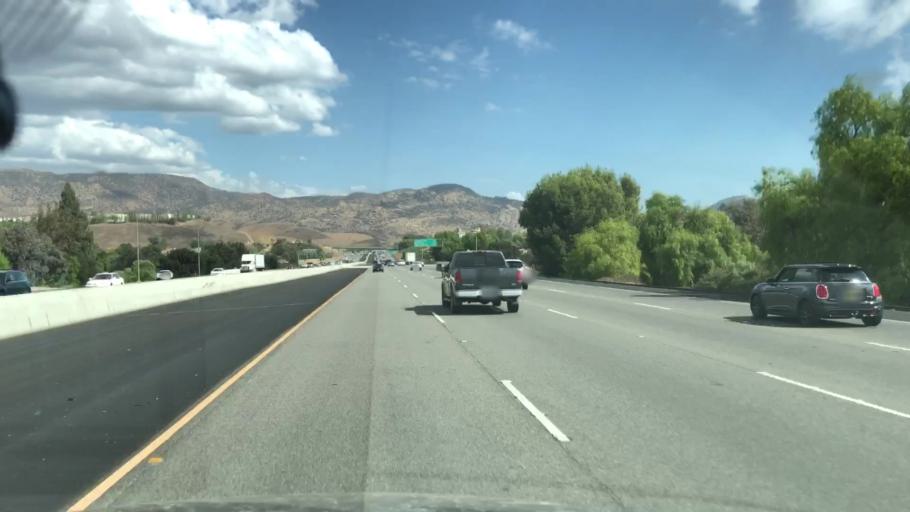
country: US
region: California
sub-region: Ventura County
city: Santa Susana
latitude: 34.2811
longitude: -118.6944
